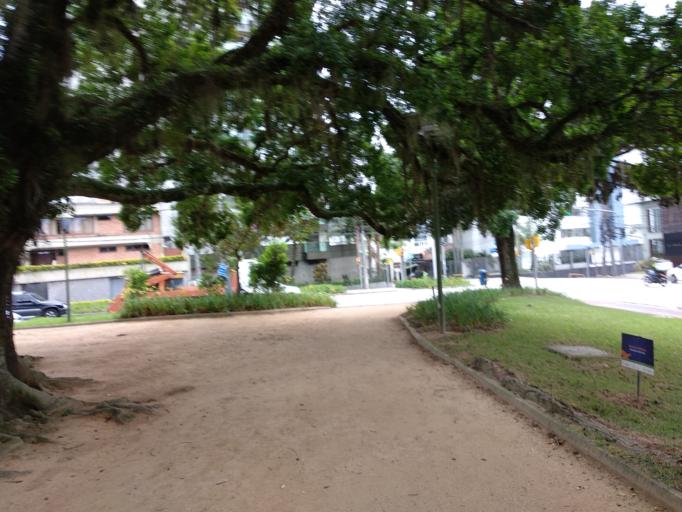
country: BR
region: Santa Catarina
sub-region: Florianopolis
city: Florianopolis
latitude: -27.5925
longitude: -48.5461
